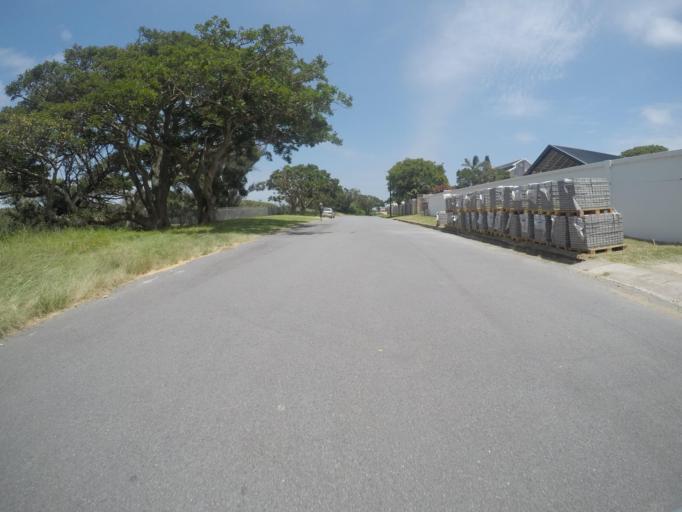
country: ZA
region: Eastern Cape
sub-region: Buffalo City Metropolitan Municipality
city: East London
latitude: -32.9975
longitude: 27.9317
